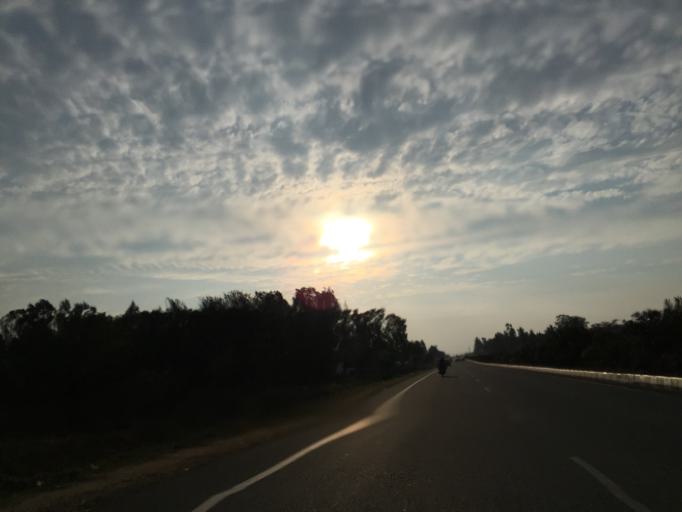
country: IN
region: Karnataka
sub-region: Kolar
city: Kolar
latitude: 13.1364
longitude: 78.1954
